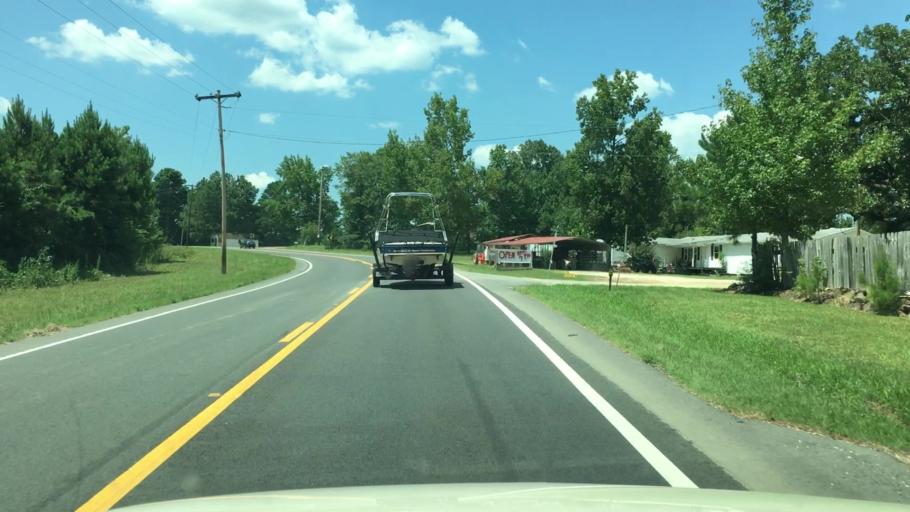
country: US
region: Arkansas
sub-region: Garland County
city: Lake Hamilton
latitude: 34.2765
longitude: -93.1508
